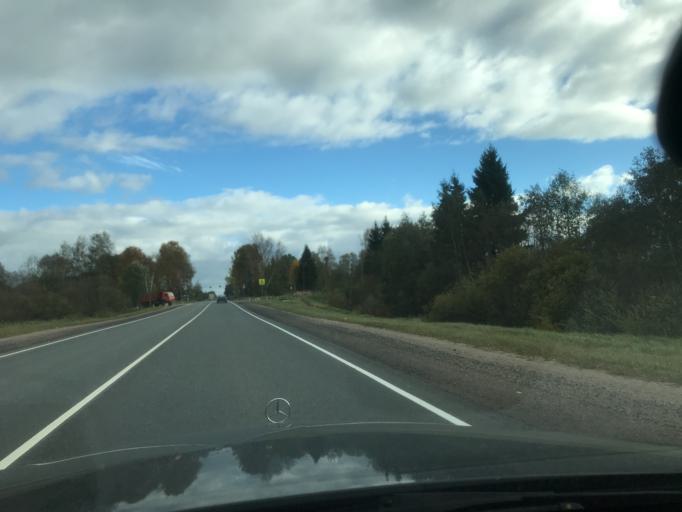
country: RU
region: Pskov
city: Opochka
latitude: 56.6641
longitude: 28.7410
